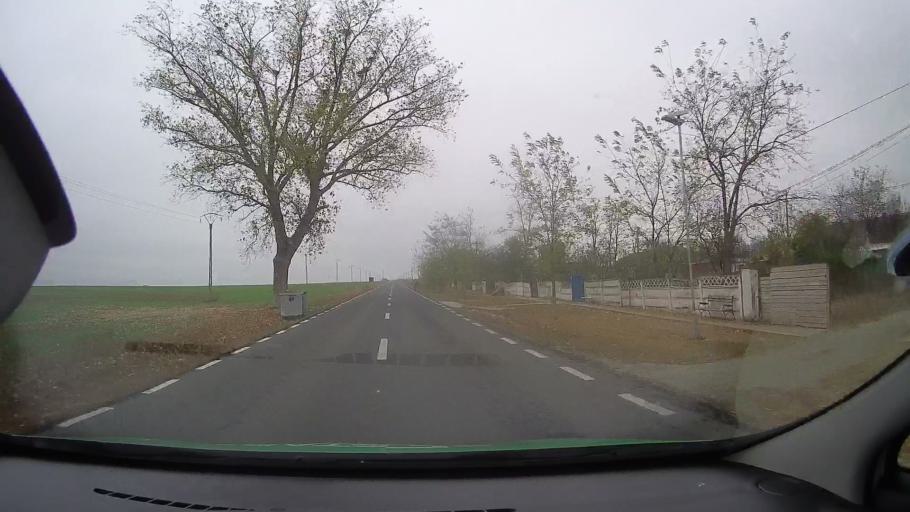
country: RO
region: Constanta
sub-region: Comuna Tortoman
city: Tortoman
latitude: 44.3502
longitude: 28.2172
